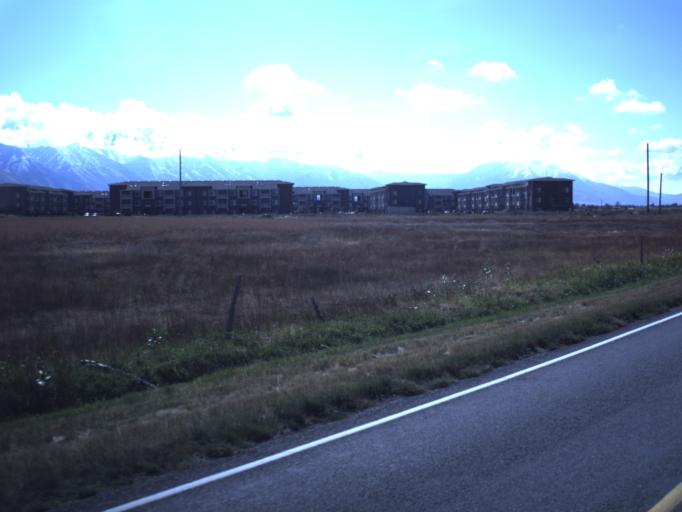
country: US
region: Utah
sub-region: Utah County
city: Spanish Fork
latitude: 40.1604
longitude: -111.6597
